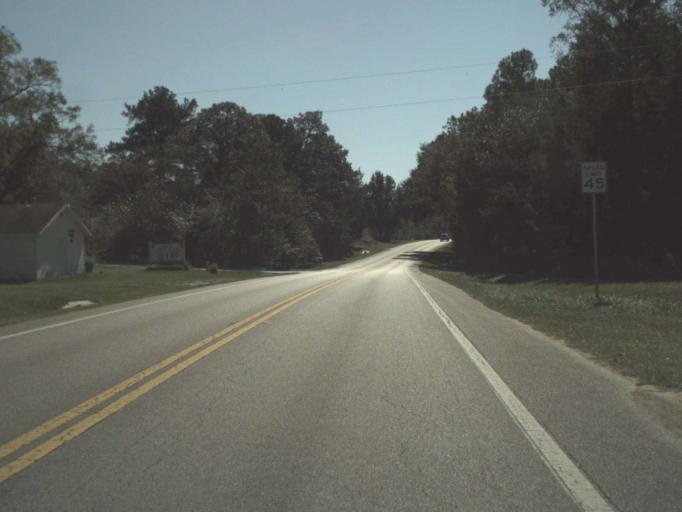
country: US
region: Florida
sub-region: Walton County
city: DeFuniak Springs
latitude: 30.8672
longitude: -86.1176
